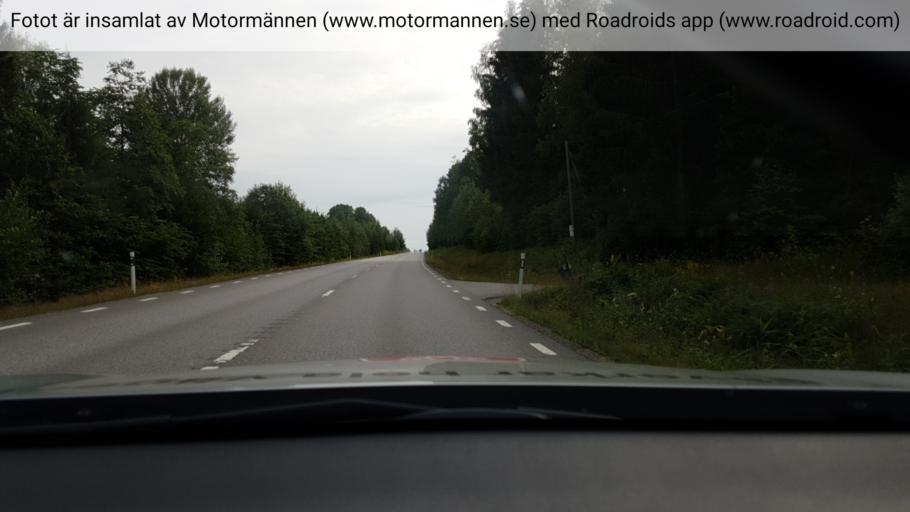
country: SE
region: Vaestra Goetaland
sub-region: Bengtsfors Kommun
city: Dals Langed
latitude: 59.0413
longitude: 12.4290
